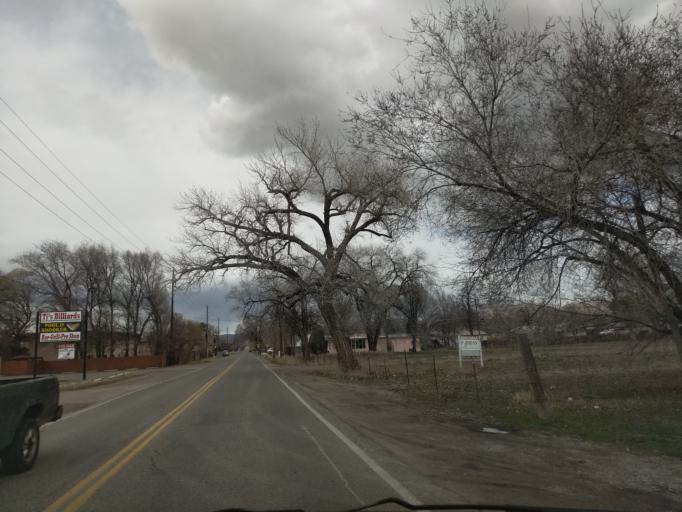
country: US
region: Colorado
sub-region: Mesa County
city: Fruitvale
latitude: 39.0783
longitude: -108.5245
